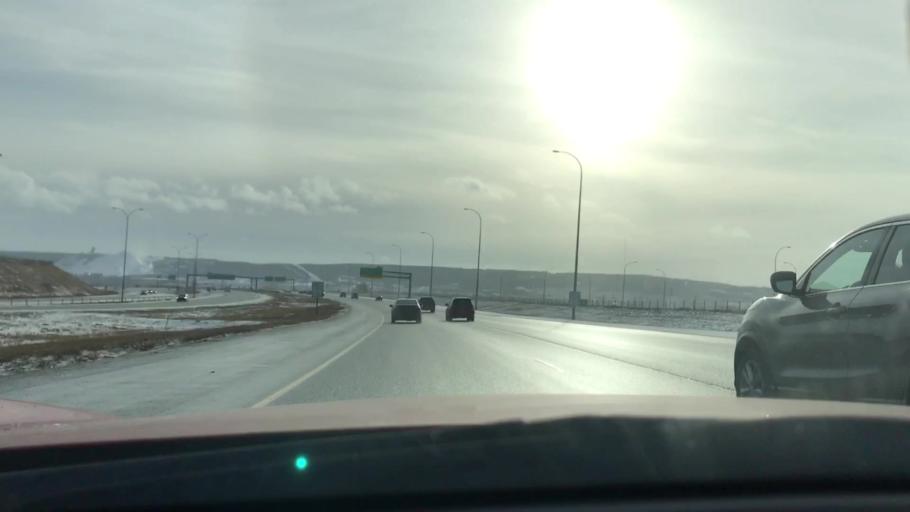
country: CA
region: Alberta
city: Calgary
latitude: 51.1245
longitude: -114.2317
